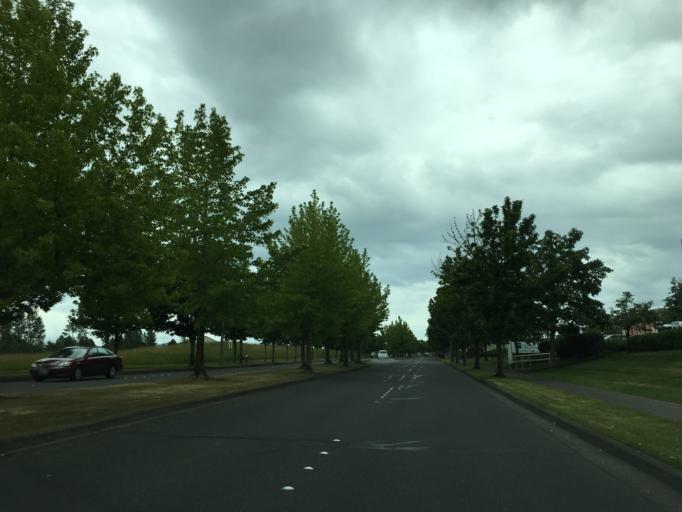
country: US
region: Washington
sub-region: Whatcom County
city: Bellingham
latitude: 48.8030
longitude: -122.4957
